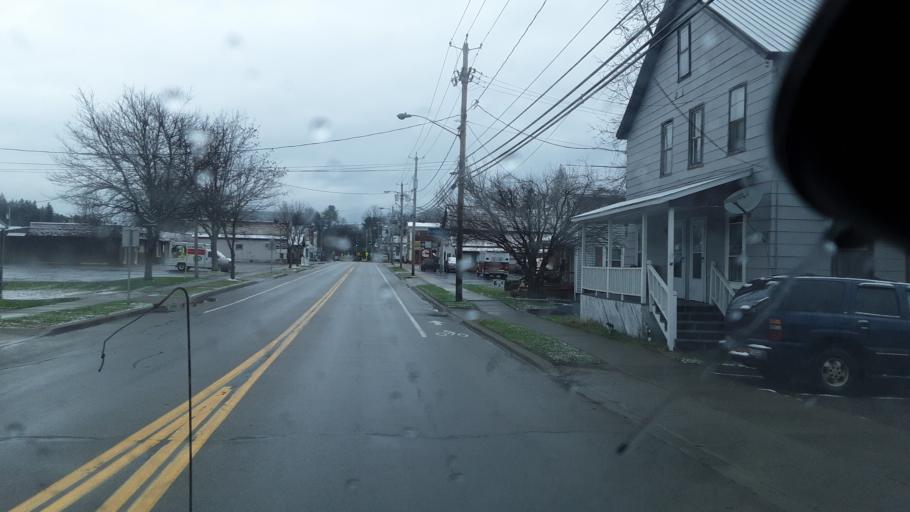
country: US
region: New York
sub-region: Cattaraugus County
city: Portville
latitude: 42.0370
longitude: -78.3392
